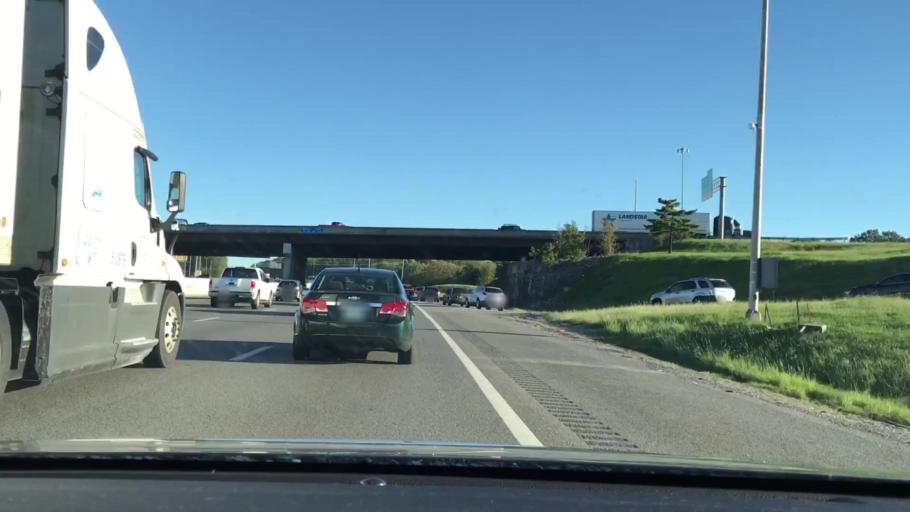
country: US
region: Tennessee
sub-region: Davidson County
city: Oak Hill
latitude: 36.1107
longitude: -86.7226
